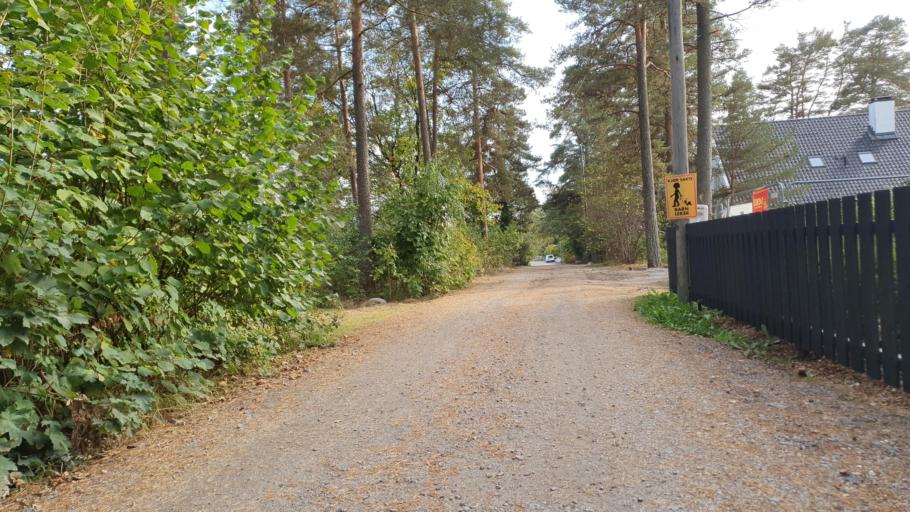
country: NO
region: Vestfold
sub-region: Tonsberg
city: Tonsberg
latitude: 59.2810
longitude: 10.4177
